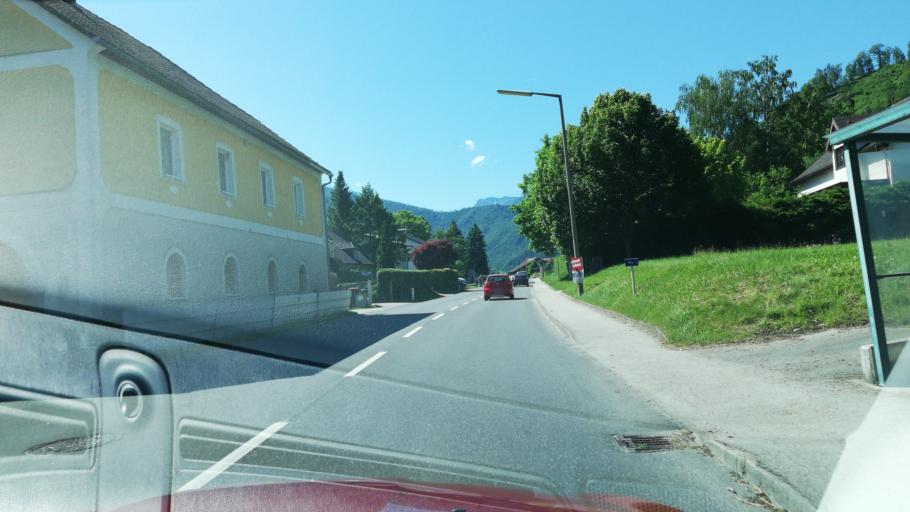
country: AT
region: Upper Austria
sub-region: Politischer Bezirk Kirchdorf an der Krems
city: Gruenburg
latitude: 47.8946
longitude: 14.2310
